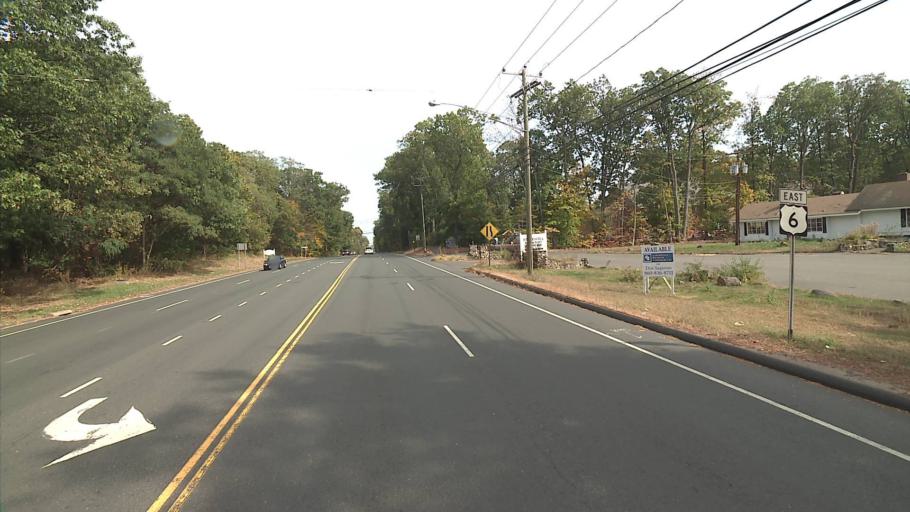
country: US
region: Connecticut
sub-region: Hartford County
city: Farmington
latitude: 41.7115
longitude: -72.8084
